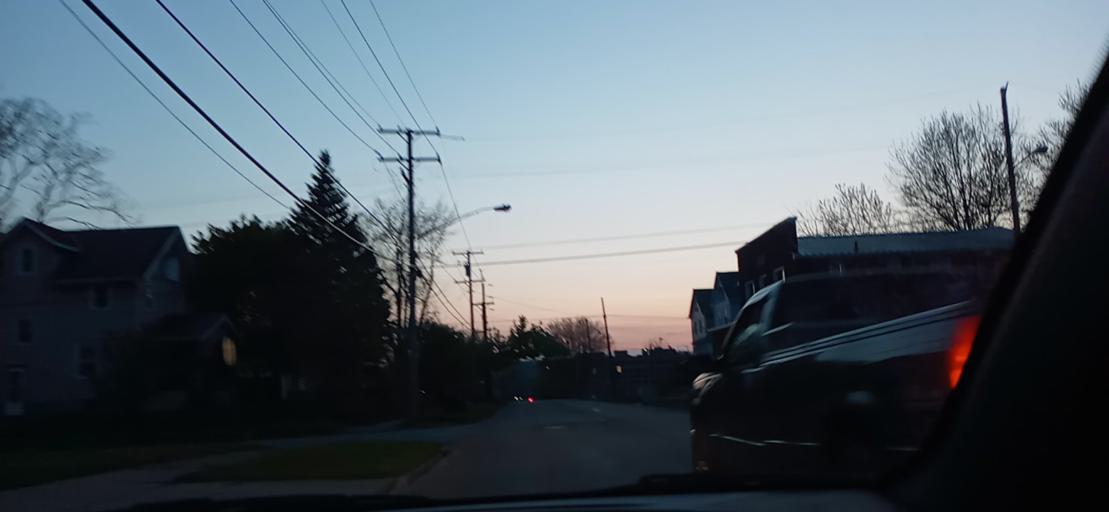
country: US
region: Ohio
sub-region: Summit County
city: Akron
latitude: 41.0508
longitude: -81.5235
